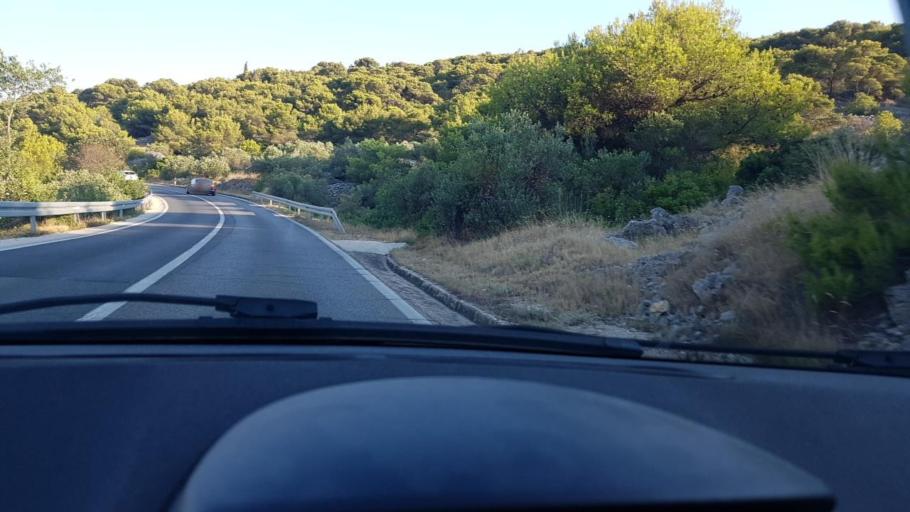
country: HR
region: Sibensko-Kniniska
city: Murter
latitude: 43.8082
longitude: 15.6049
